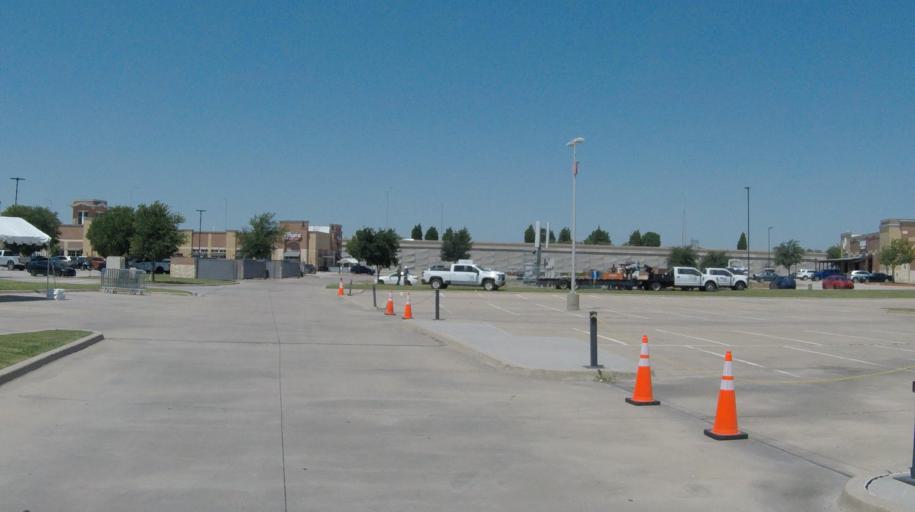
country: US
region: Texas
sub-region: Collin County
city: Frisco
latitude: 33.1539
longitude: -96.8381
